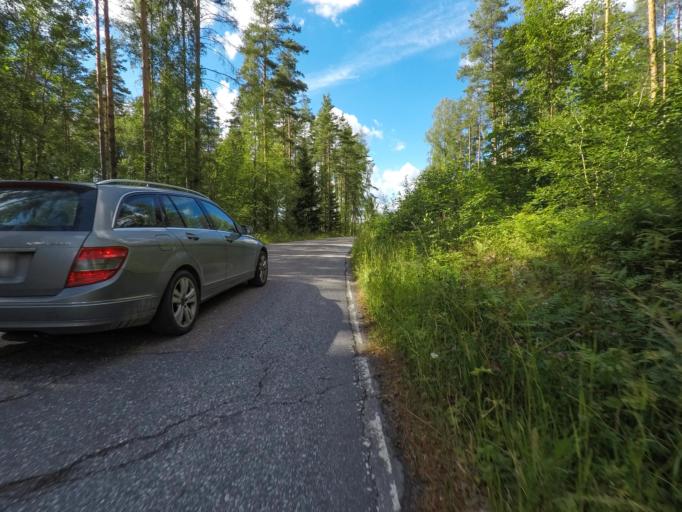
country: FI
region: South Karelia
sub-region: Lappeenranta
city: Joutseno
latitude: 61.1080
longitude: 28.3713
